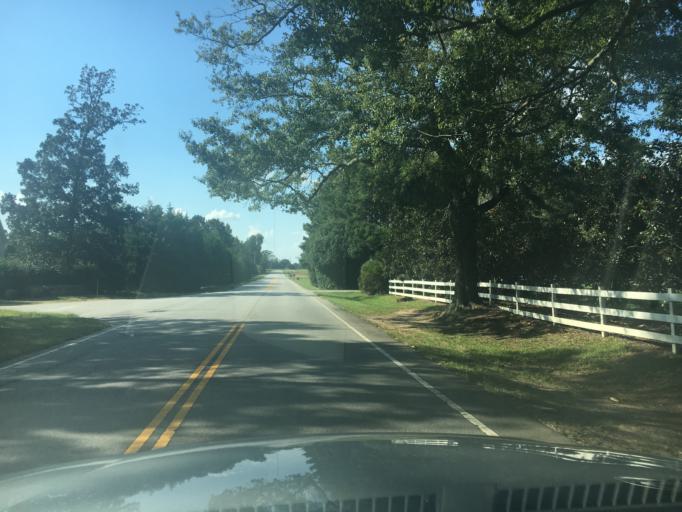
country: US
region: South Carolina
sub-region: Greenville County
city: Fountain Inn
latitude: 34.6325
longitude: -82.2526
